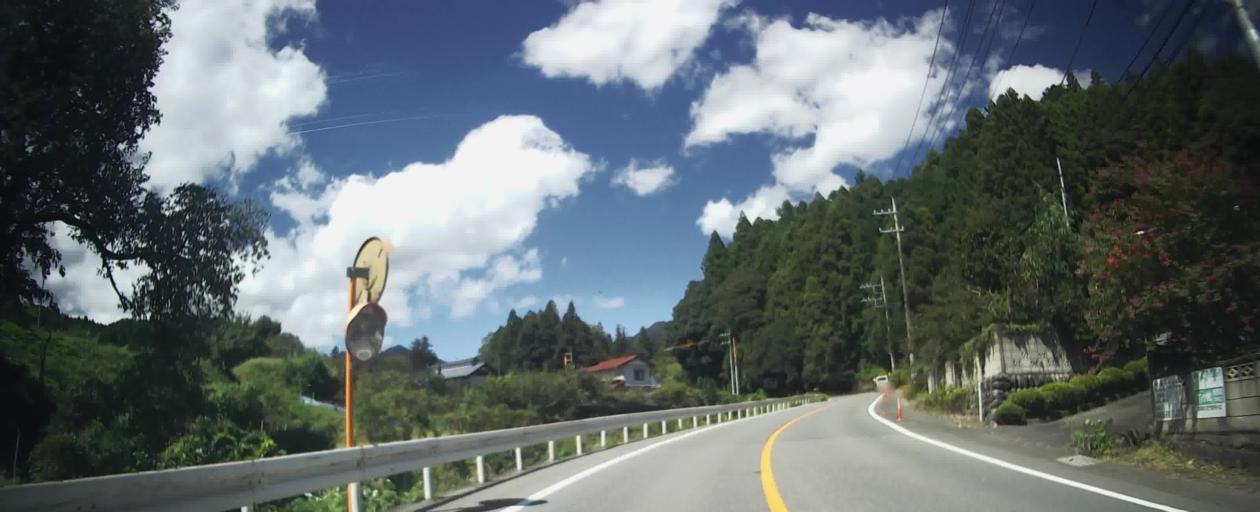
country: JP
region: Gunma
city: Kanekomachi
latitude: 36.4245
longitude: 138.9329
